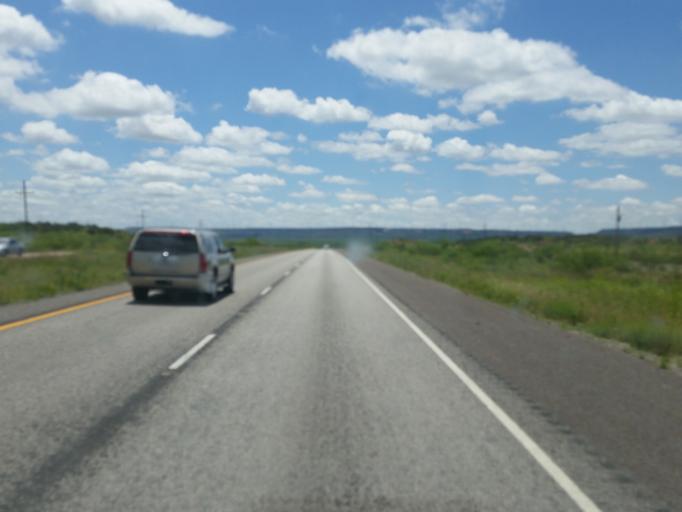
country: US
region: Texas
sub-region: Garza County
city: Post
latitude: 33.0207
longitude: -101.1810
